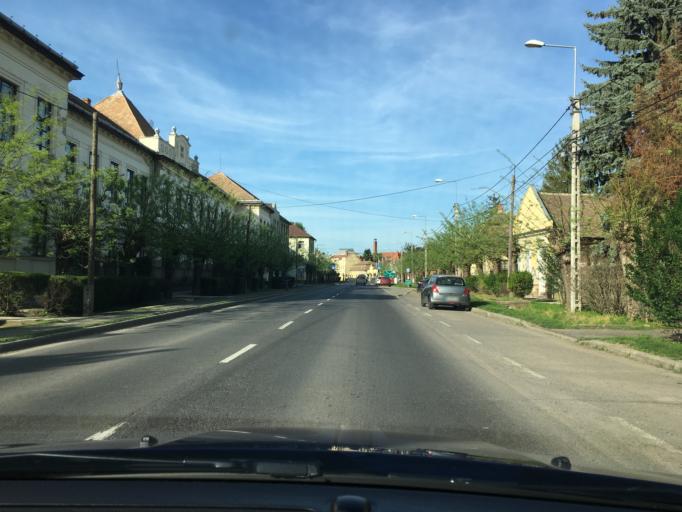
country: HU
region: Bekes
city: Mezobereny
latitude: 46.8209
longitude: 21.0266
